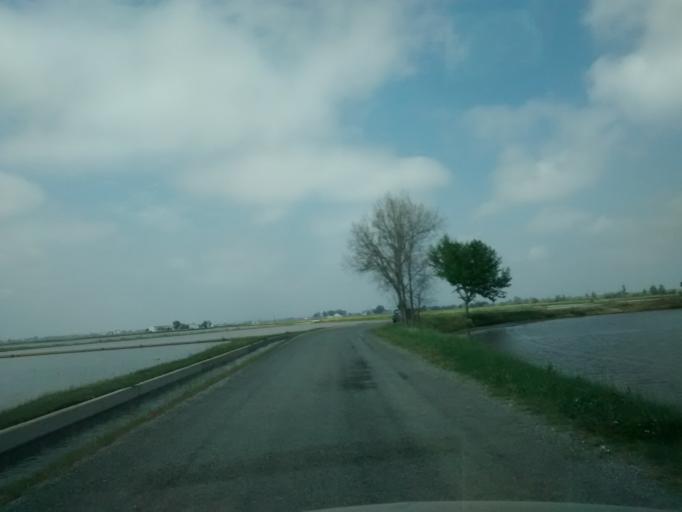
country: ES
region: Catalonia
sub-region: Provincia de Tarragona
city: Deltebre
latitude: 40.6899
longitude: 0.7801
